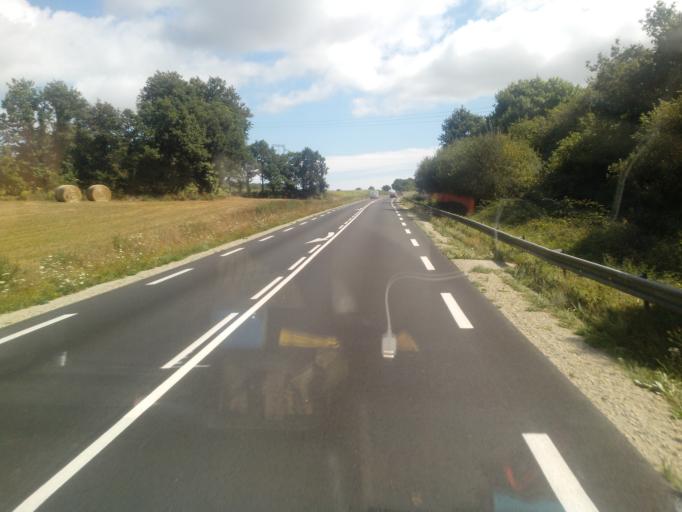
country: FR
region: Brittany
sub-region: Departement du Morbihan
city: Peaule
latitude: 47.5967
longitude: -2.3804
